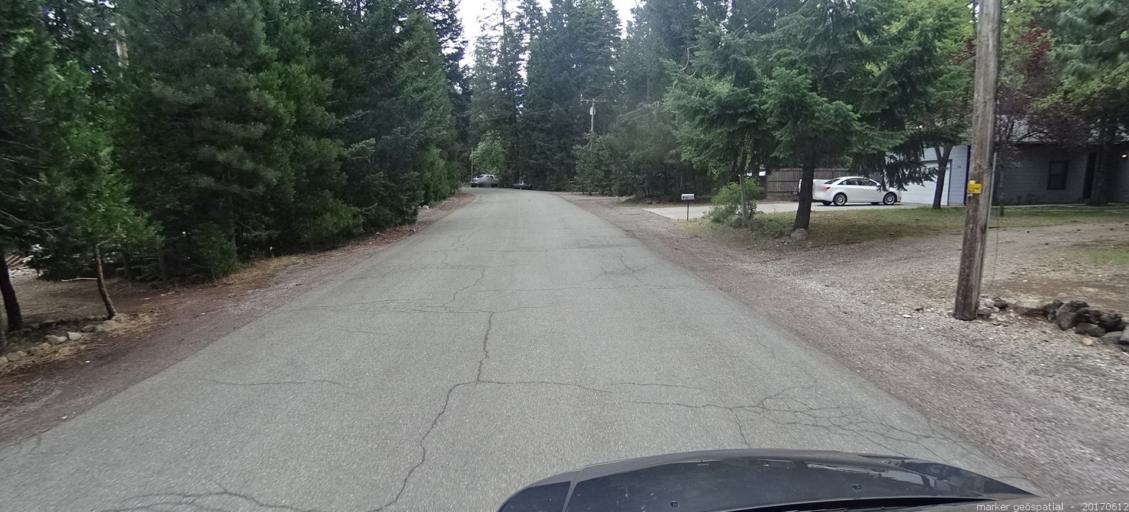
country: US
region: California
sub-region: Siskiyou County
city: Mount Shasta
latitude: 41.3462
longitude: -122.3554
